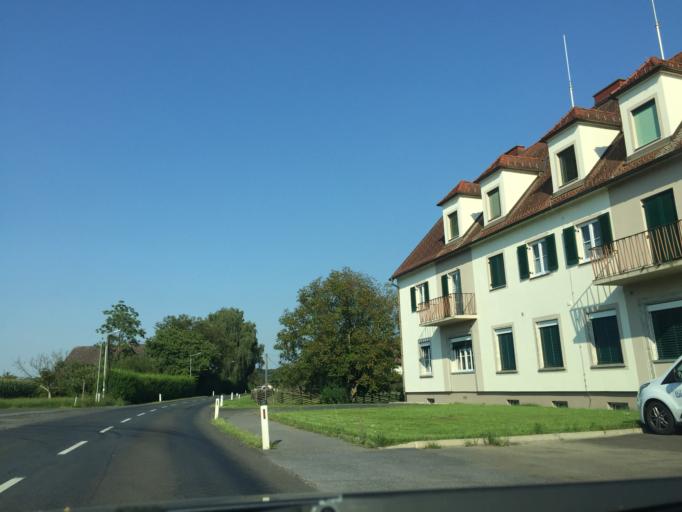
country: AT
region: Styria
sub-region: Politischer Bezirk Suedoststeiermark
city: Deutsch Goritz
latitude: 46.7531
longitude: 15.8321
